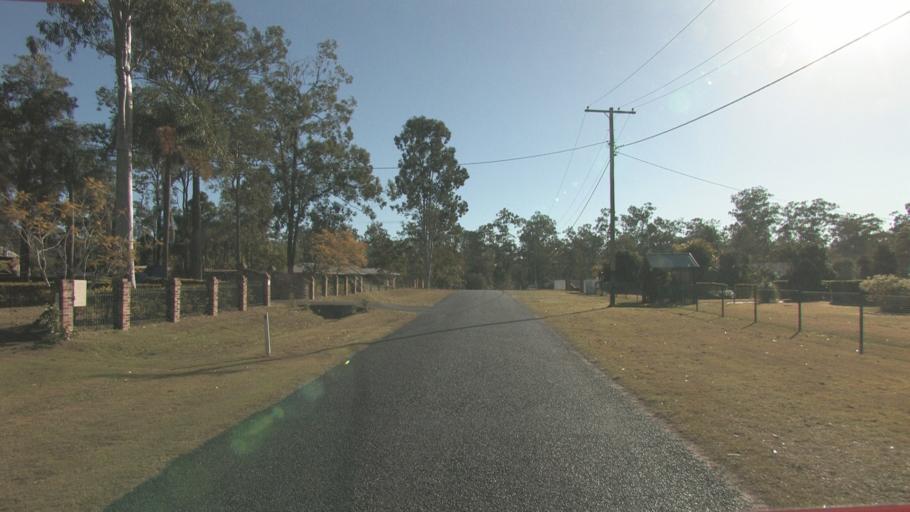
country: AU
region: Queensland
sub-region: Logan
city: North Maclean
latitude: -27.7455
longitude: 153.0097
